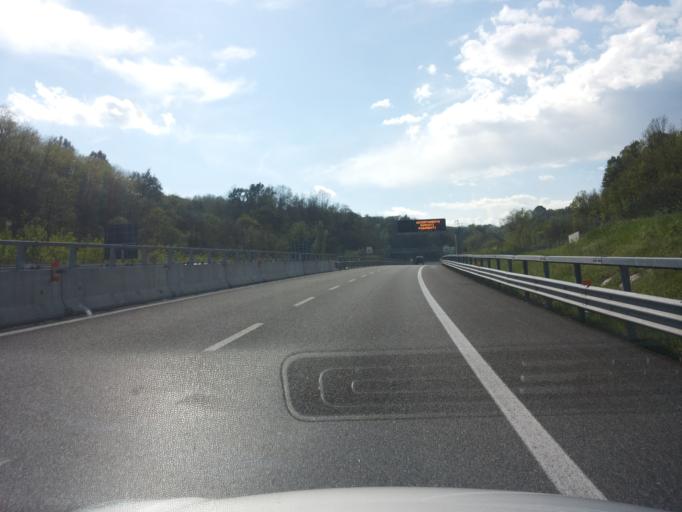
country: IT
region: Lombardy
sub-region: Provincia di Varese
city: Lozza
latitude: 45.7722
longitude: 8.8588
